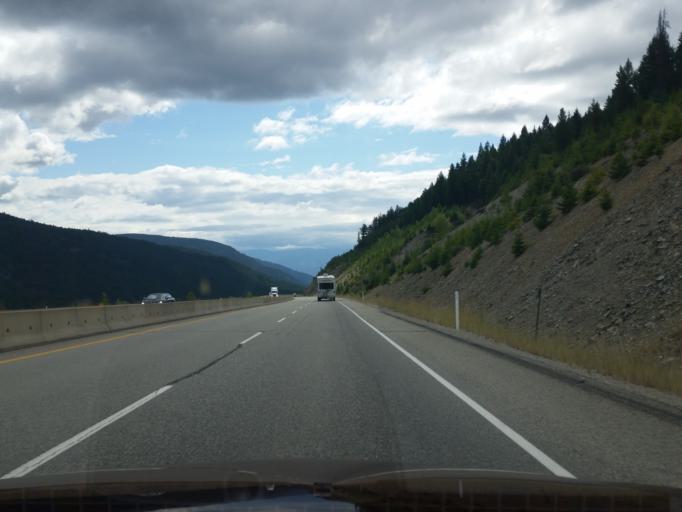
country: CA
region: British Columbia
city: Peachland
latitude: 49.8613
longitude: -119.8550
